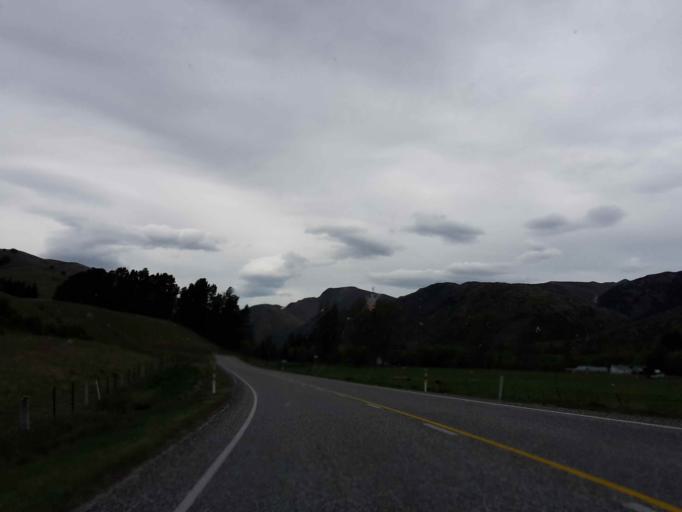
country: NZ
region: Otago
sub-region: Queenstown-Lakes District
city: Wanaka
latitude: -44.6459
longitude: 169.5000
